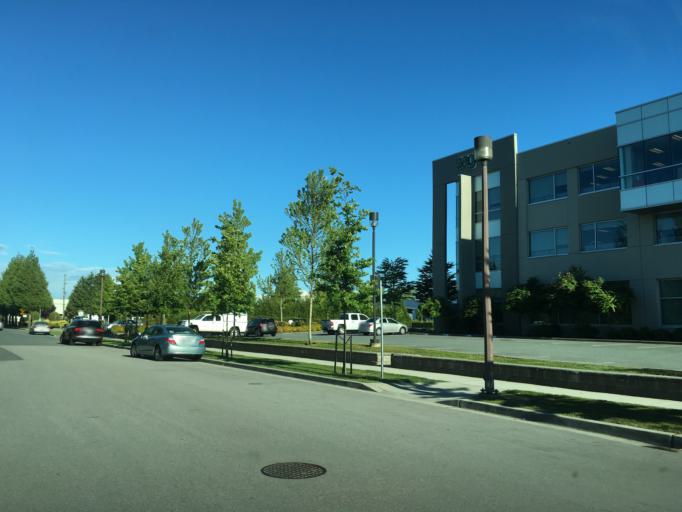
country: CA
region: British Columbia
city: Richmond
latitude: 49.1719
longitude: -123.0718
